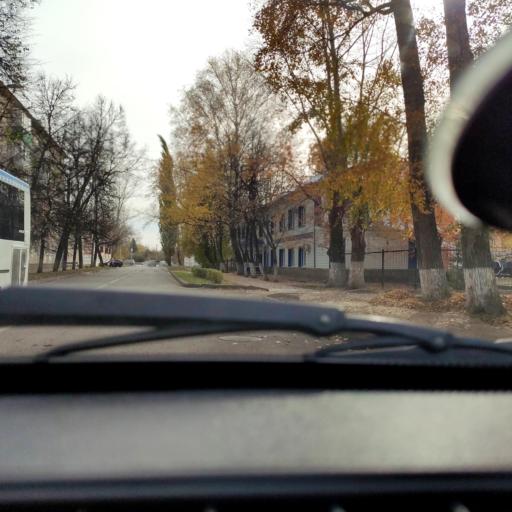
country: RU
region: Bashkortostan
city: Mikhaylovka
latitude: 54.7020
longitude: 55.8373
